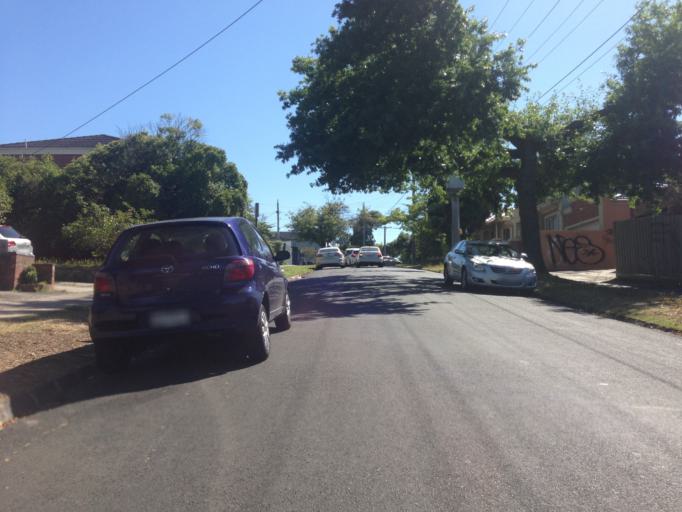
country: AU
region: Victoria
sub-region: Boroondara
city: Balwyn North
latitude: -37.7947
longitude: 145.0776
